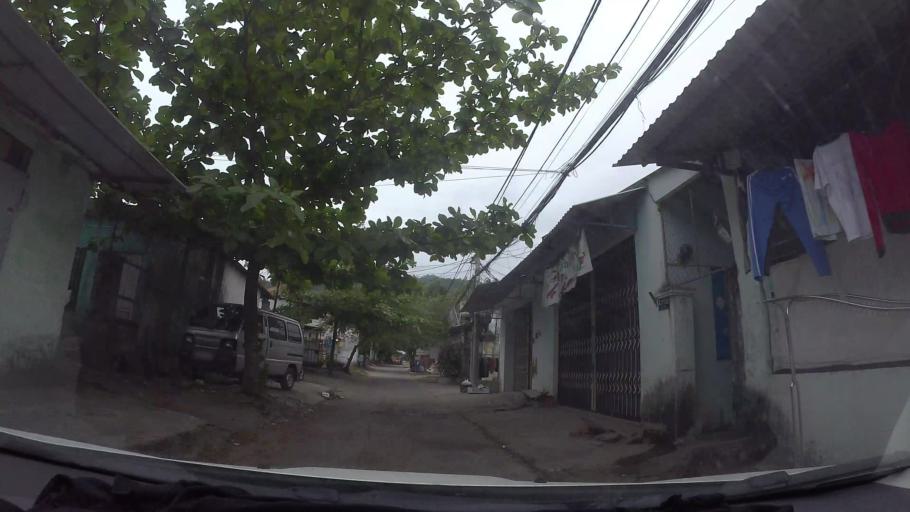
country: VN
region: Da Nang
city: Lien Chieu
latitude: 16.0715
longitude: 108.1376
